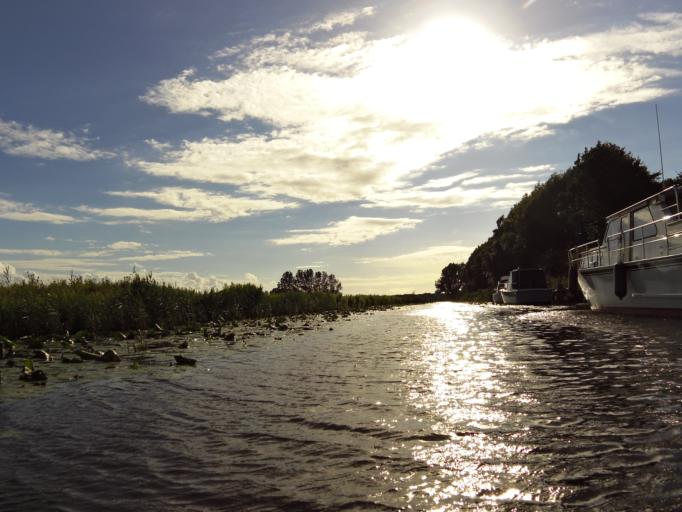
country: NL
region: South Holland
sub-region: Gemeente Wassenaar
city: Wassenaar
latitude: 52.1611
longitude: 4.4162
